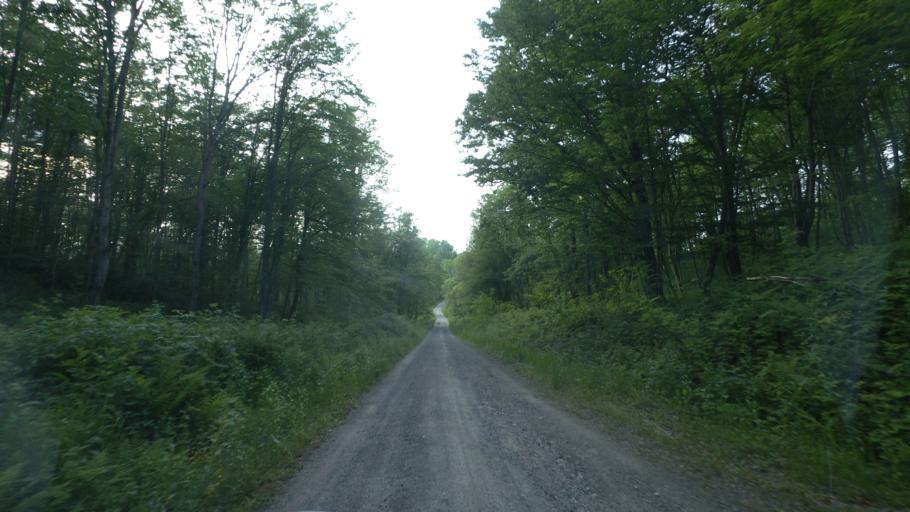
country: HR
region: Sisacko-Moslavacka
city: Gvozd
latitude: 45.3062
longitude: 15.9803
